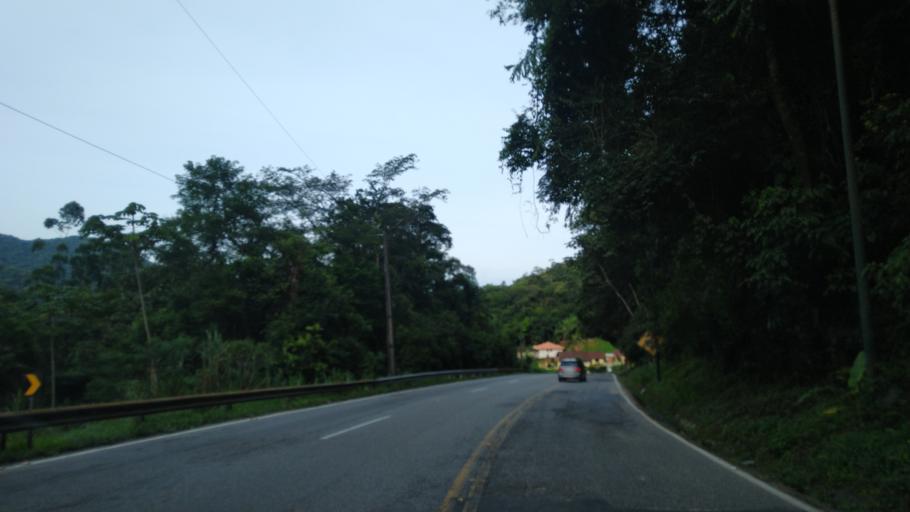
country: BR
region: Santa Catarina
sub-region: Joinville
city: Joinville
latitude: -26.1826
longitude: -49.0181
